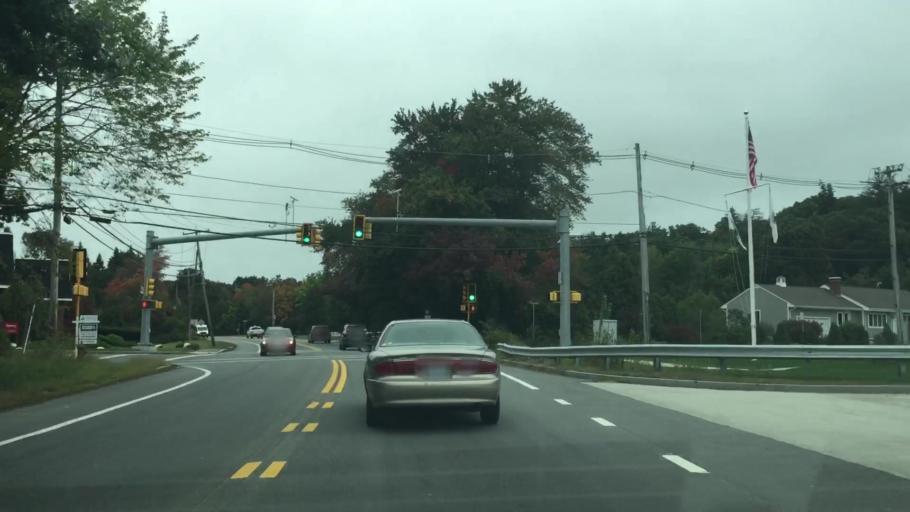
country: US
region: Massachusetts
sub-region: Essex County
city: North Andover
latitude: 42.7042
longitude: -71.1171
